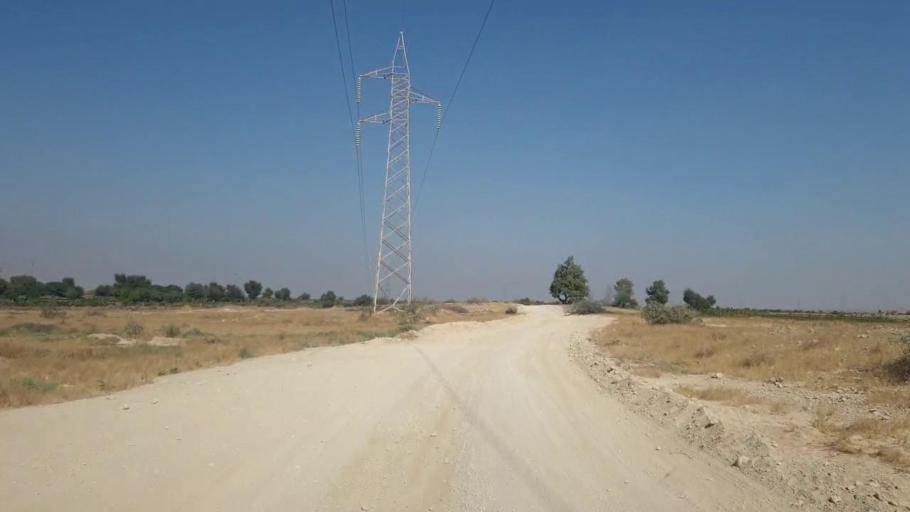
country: PK
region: Sindh
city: Thatta
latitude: 25.2481
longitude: 67.8047
